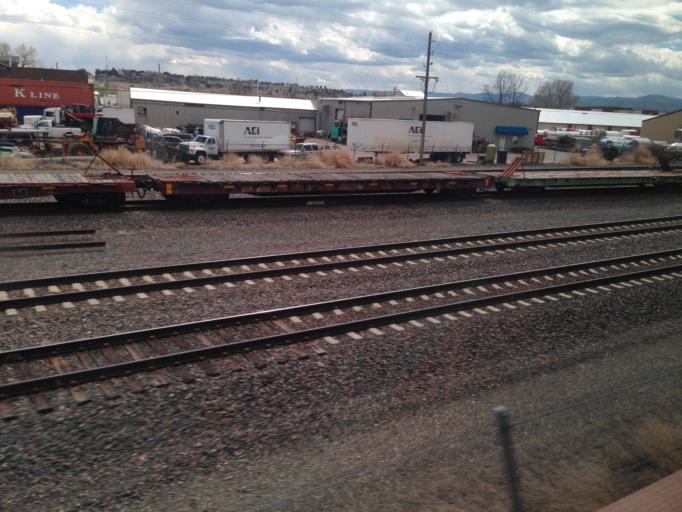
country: US
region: Colorado
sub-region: Adams County
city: Berkley
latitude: 39.8026
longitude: -105.0542
